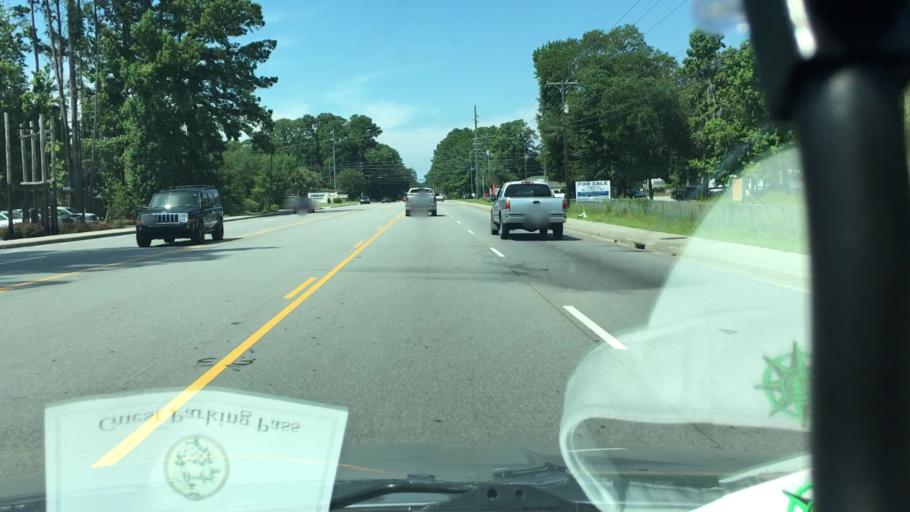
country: US
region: South Carolina
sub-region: Beaufort County
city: Burton
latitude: 32.4290
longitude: -80.7212
